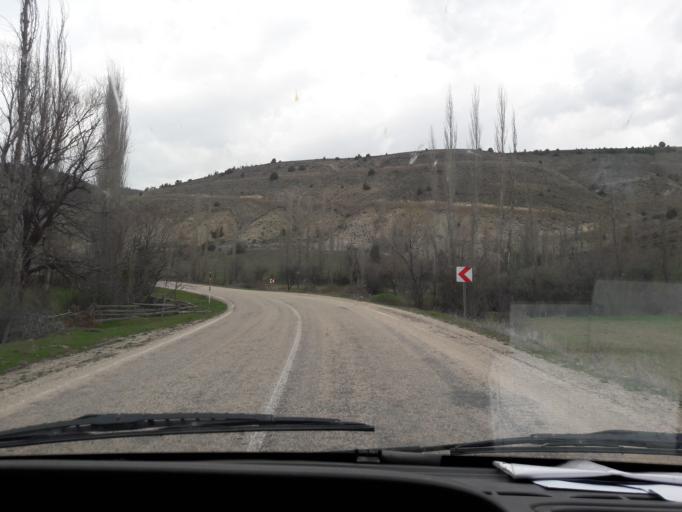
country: TR
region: Giresun
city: Alucra
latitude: 40.2862
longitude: 38.8199
